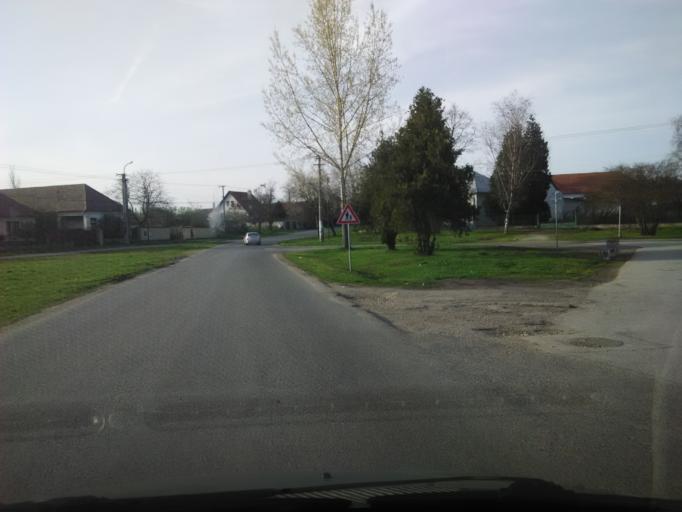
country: SK
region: Nitriansky
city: Surany
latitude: 48.0687
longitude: 18.2004
